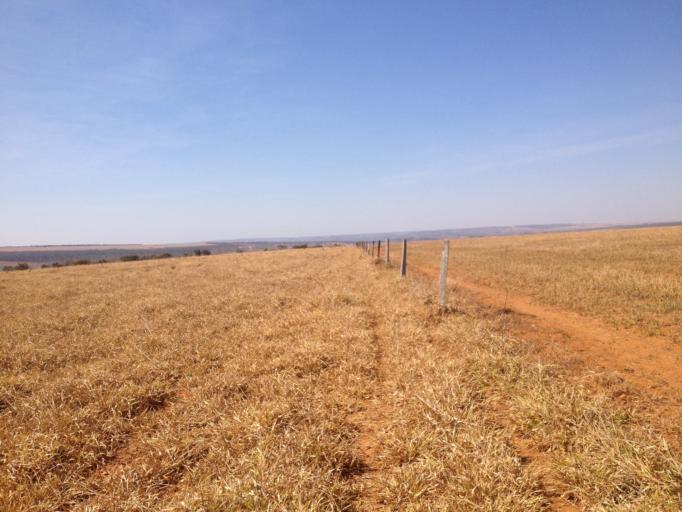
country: BR
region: Minas Gerais
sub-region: Unai
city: Unai
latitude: -16.1381
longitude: -47.3667
